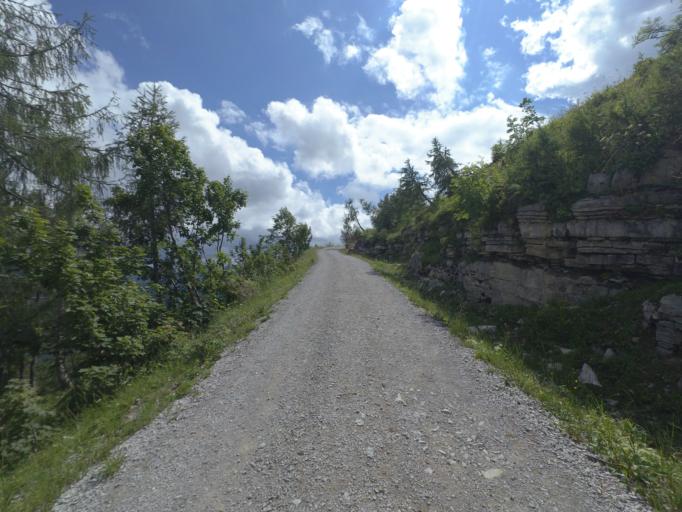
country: AT
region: Salzburg
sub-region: Politischer Bezirk Salzburg-Umgebung
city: Hintersee
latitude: 47.6568
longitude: 13.2955
